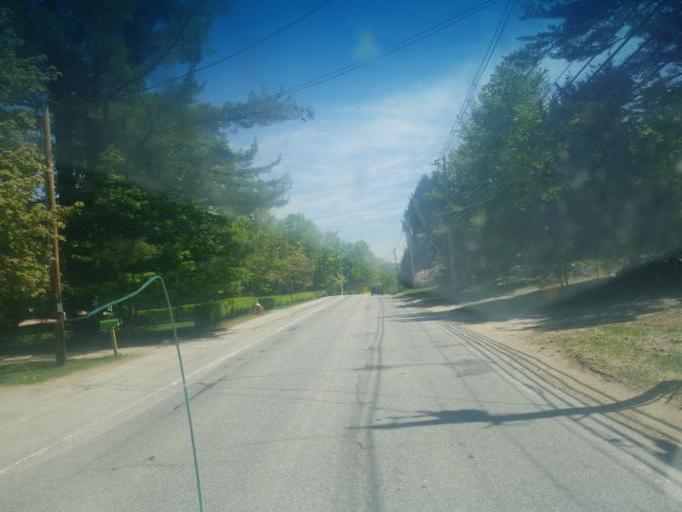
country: US
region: New Hampshire
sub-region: Grafton County
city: Plymouth
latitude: 43.7611
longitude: -71.7037
